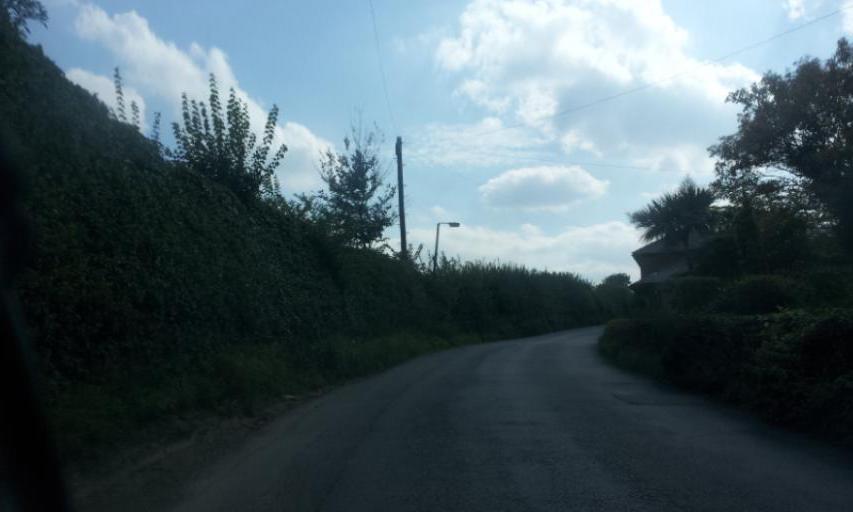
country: GB
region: England
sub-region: Kent
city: Maidstone
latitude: 51.2538
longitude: 0.5133
